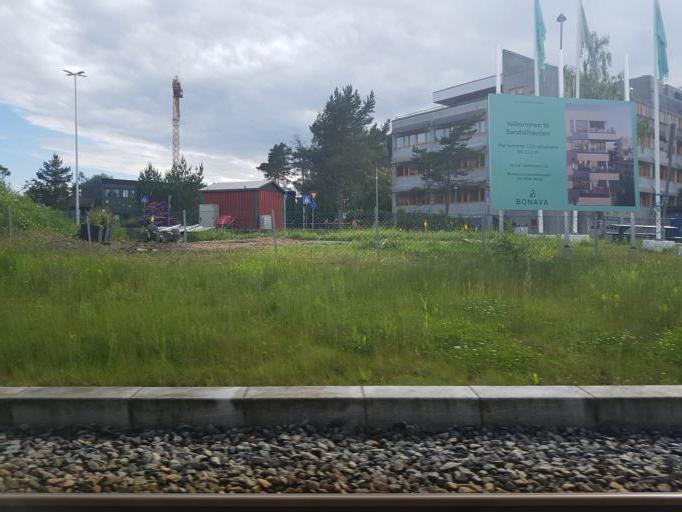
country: NO
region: Hordaland
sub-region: Bergen
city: Ytrebygda
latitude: 60.2973
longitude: 5.2791
